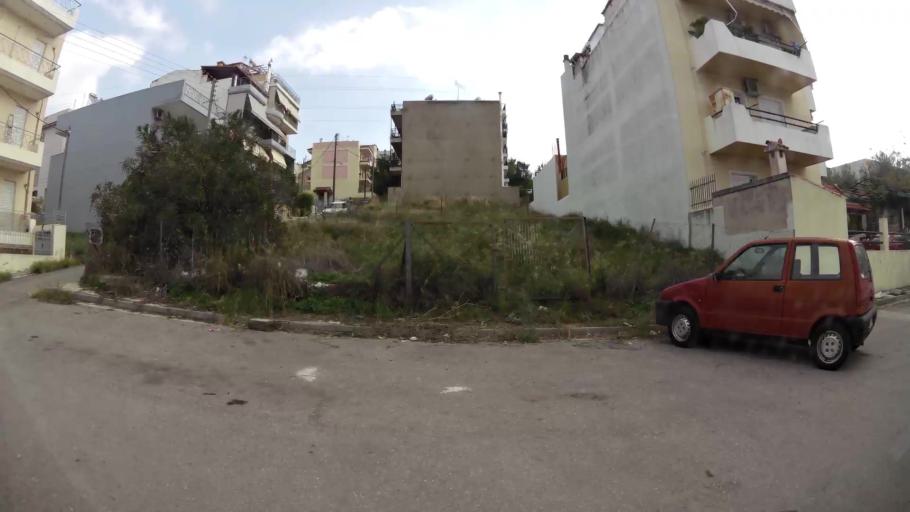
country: GR
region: Attica
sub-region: Nomarchia Dytikis Attikis
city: Zefyri
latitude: 38.0594
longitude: 23.7202
